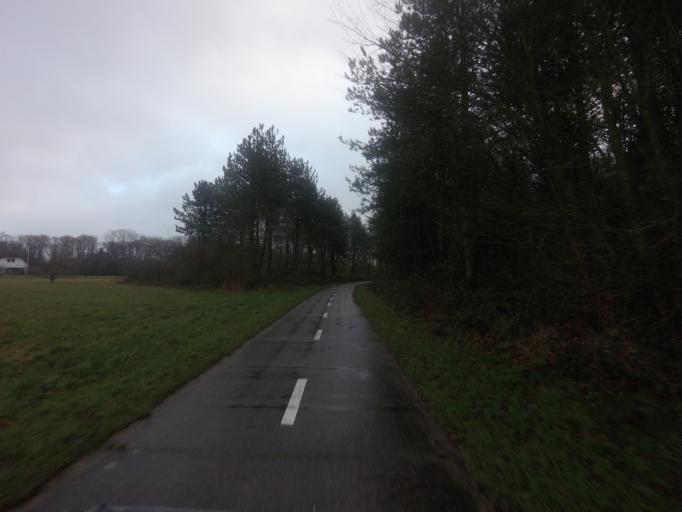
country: NL
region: North Holland
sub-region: Gemeente Texel
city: Den Burg
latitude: 53.1524
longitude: 4.8638
